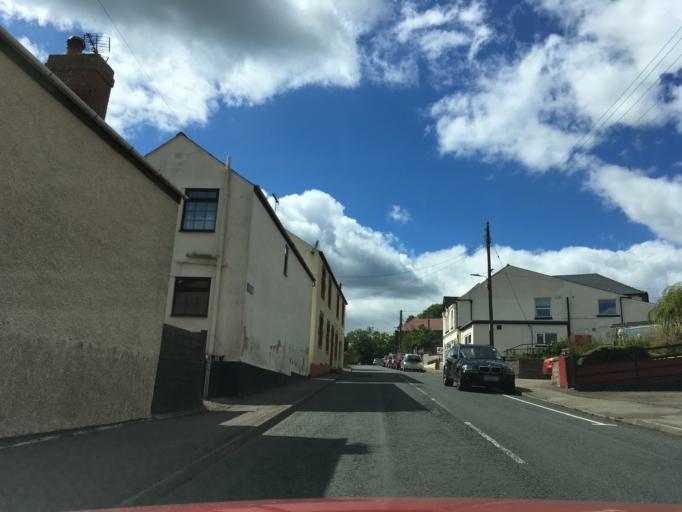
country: GB
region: England
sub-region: Gloucestershire
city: Bream
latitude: 51.7535
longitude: -2.5728
